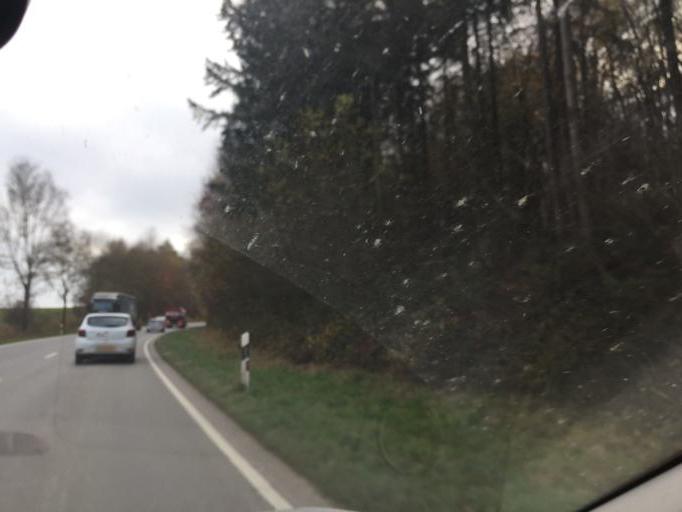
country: LU
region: Diekirch
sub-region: Canton de Redange
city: Saeul
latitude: 49.7417
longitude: 5.9809
